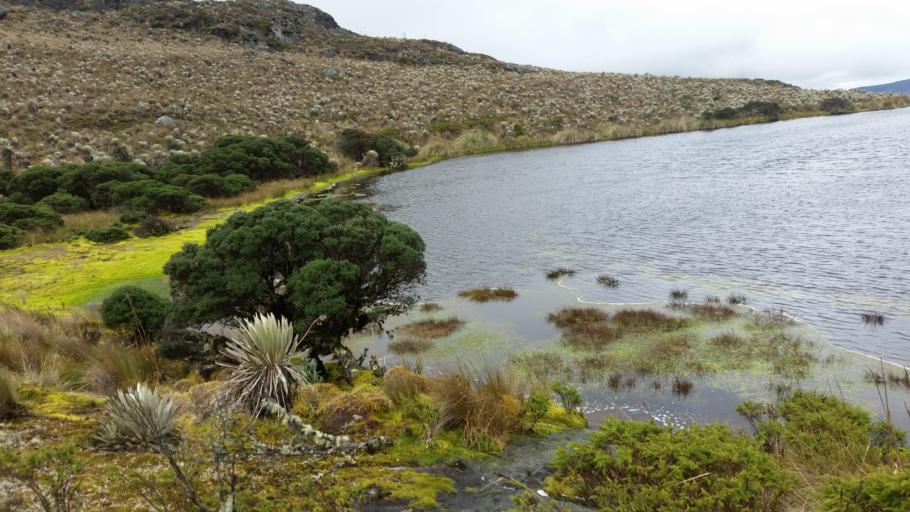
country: CO
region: Cundinamarca
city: Pasca
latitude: 4.3714
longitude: -74.2127
